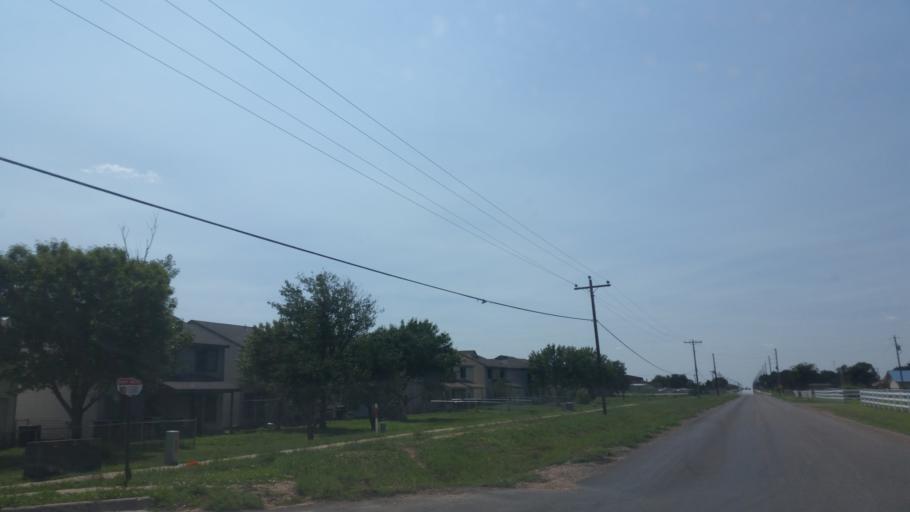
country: US
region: New Mexico
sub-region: Curry County
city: Clovis
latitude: 34.4484
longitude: -103.1733
